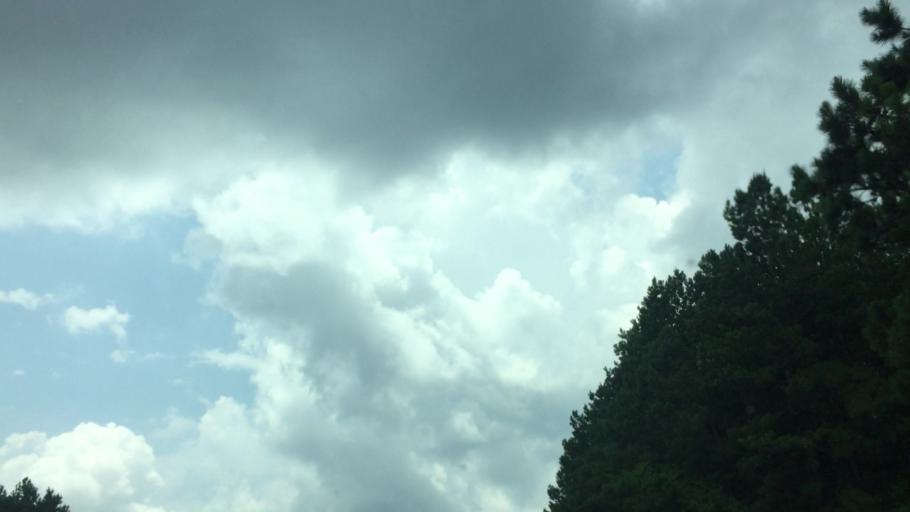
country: US
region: Georgia
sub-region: Fulton County
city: Fairburn
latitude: 33.5978
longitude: -84.6377
